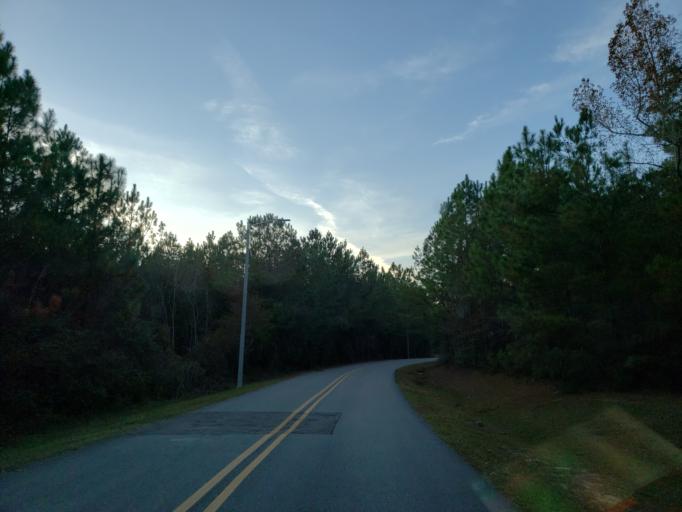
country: US
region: Mississippi
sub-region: Forrest County
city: Hattiesburg
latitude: 31.2786
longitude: -89.3108
